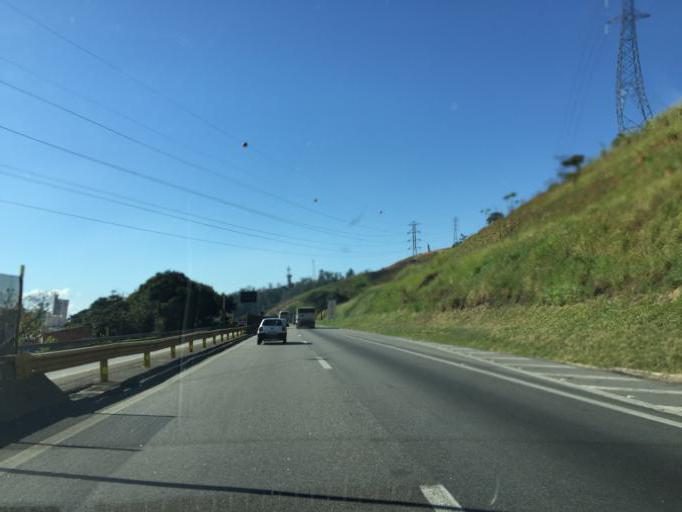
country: BR
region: Sao Paulo
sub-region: Aparecida
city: Aparecida
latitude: -22.8578
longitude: -45.2325
